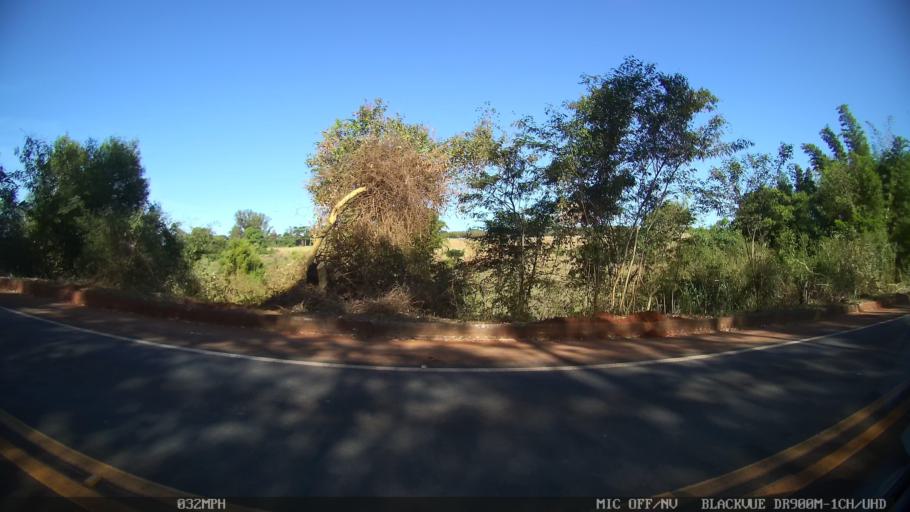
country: BR
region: Sao Paulo
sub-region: Olimpia
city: Olimpia
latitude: -20.7363
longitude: -48.8782
